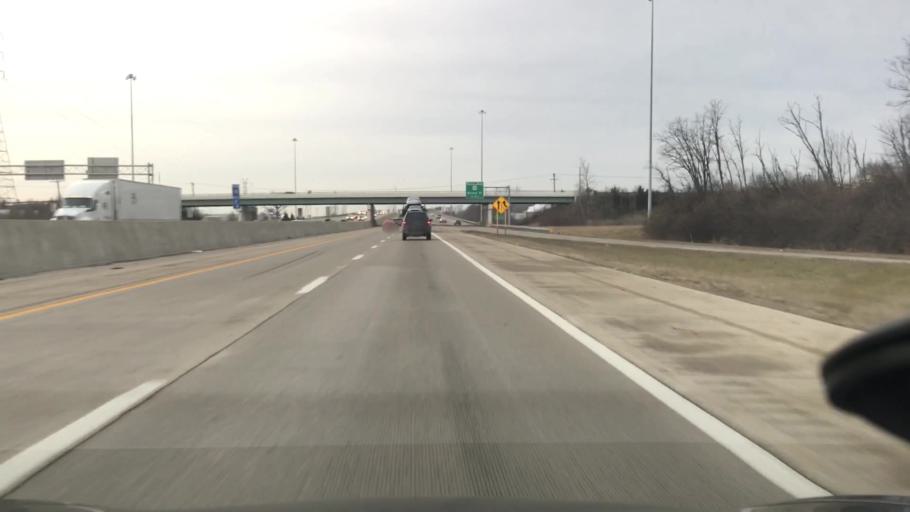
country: US
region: Ohio
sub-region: Franklin County
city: Lincoln Village
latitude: 39.9726
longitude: -83.1194
